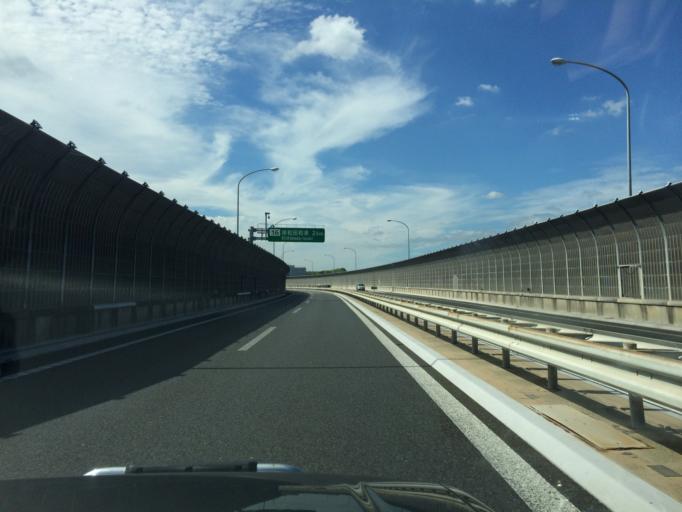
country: JP
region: Osaka
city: Izumi
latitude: 34.4572
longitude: 135.4492
